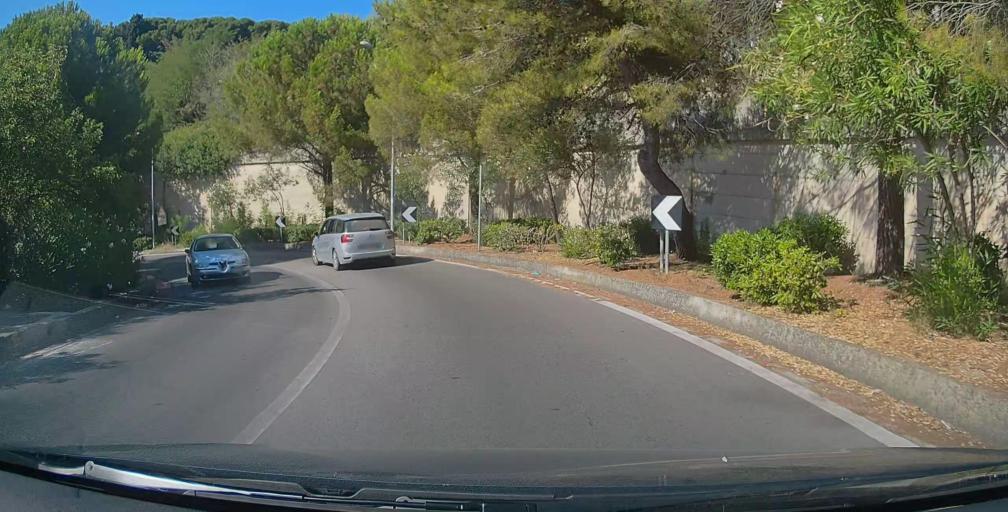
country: IT
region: Sicily
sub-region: Messina
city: Capo d'Orlando
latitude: 38.1566
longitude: 14.7521
